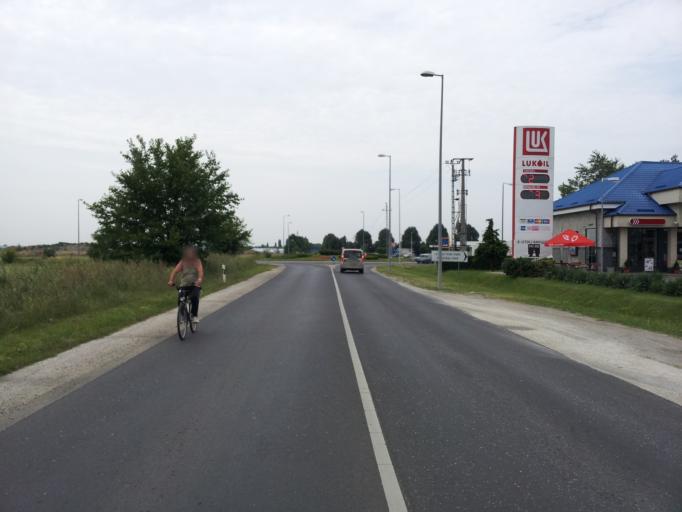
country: HU
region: Pest
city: Szigetszentmiklos
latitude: 47.3709
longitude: 19.0485
